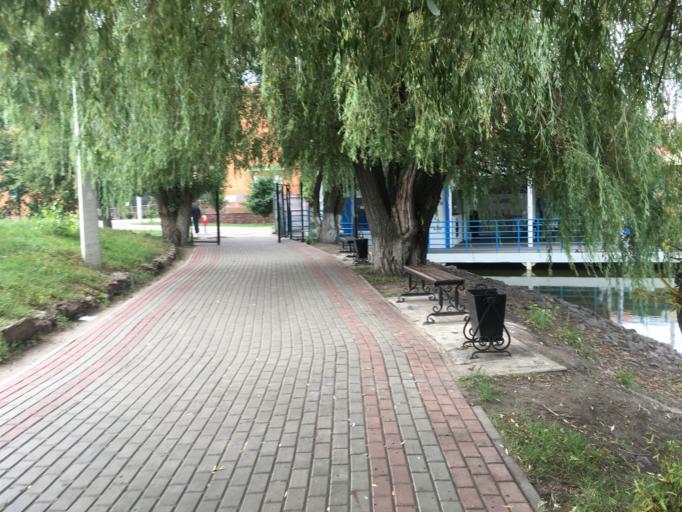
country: RU
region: Voronezj
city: Rossosh'
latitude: 50.1975
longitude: 39.5753
